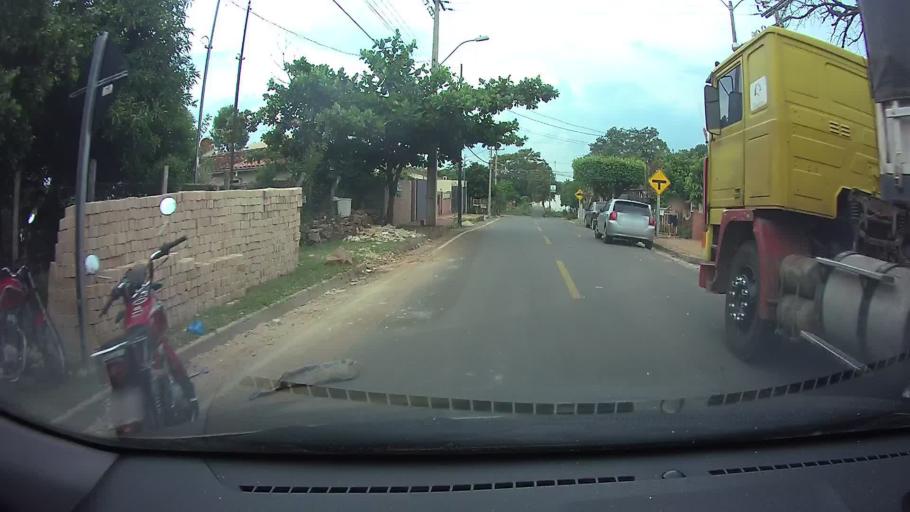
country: PY
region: Central
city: San Lorenzo
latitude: -25.2734
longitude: -57.4665
